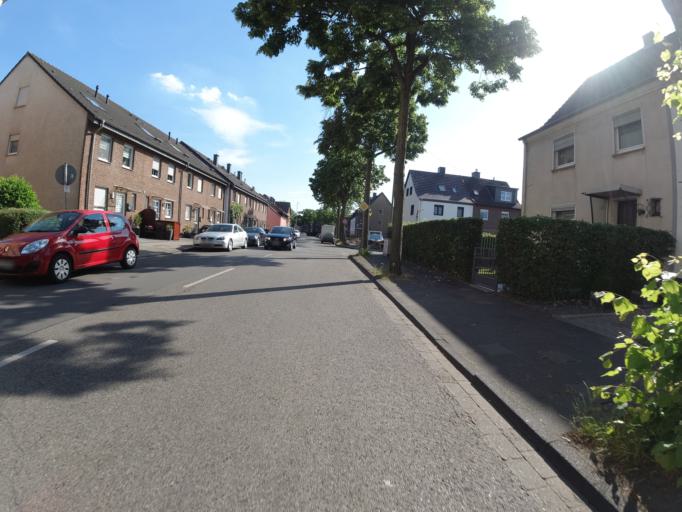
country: DE
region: North Rhine-Westphalia
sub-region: Regierungsbezirk Dusseldorf
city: Hochfeld
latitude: 51.3912
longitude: 6.7136
